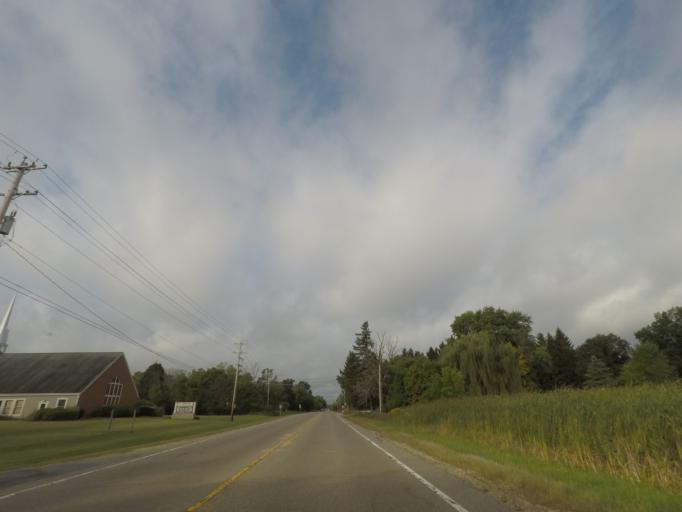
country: US
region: Wisconsin
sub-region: Waukesha County
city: Dousman
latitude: 43.0244
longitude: -88.4782
